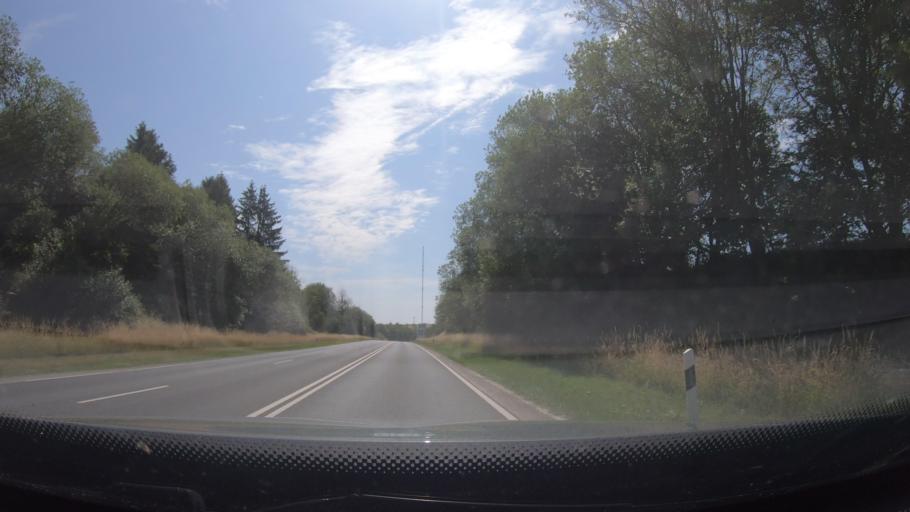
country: LU
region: Diekirch
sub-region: Canton de Clervaux
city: Hosingen
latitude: 50.0297
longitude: 6.0843
